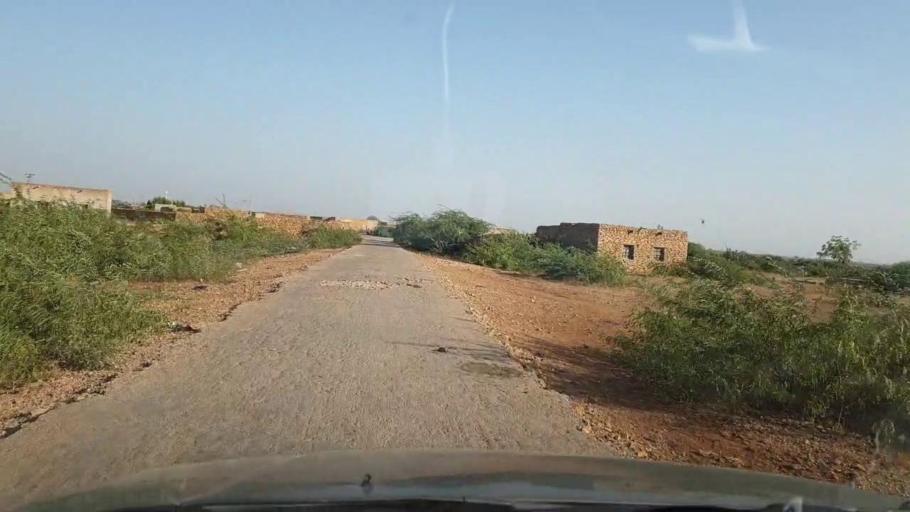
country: PK
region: Sindh
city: Kotri
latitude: 25.1324
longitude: 68.2299
